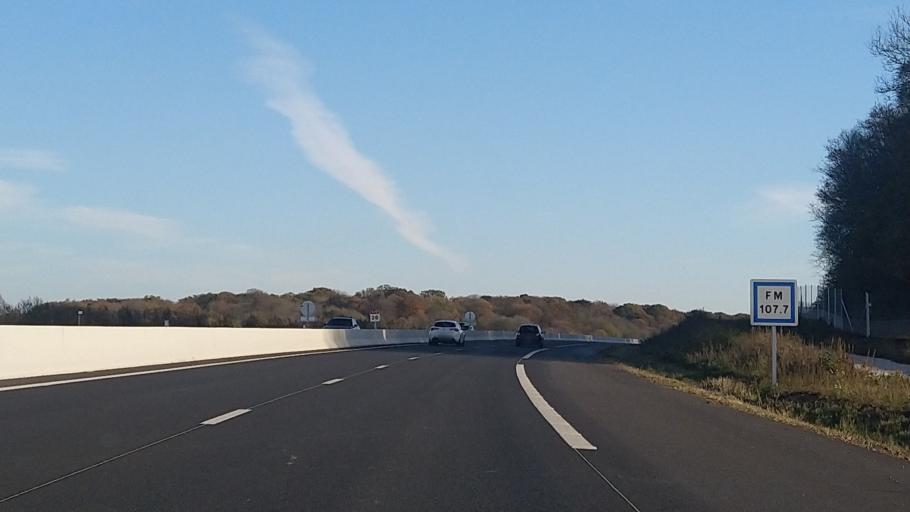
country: FR
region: Ile-de-France
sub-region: Departement du Val-d'Oise
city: Maffliers
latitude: 49.0977
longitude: 2.2929
